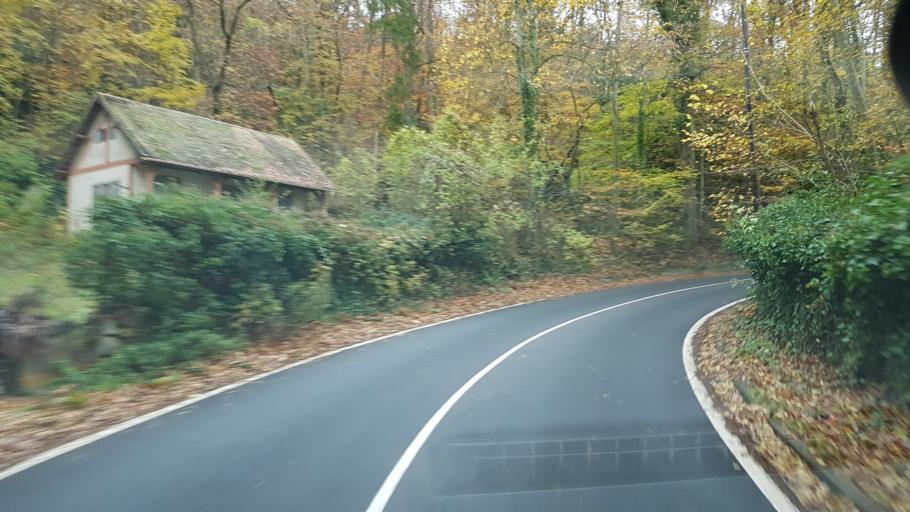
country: FR
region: Ile-de-France
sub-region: Departement des Yvelines
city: Dampierre-en-Yvelines
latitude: 48.7114
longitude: 1.9916
